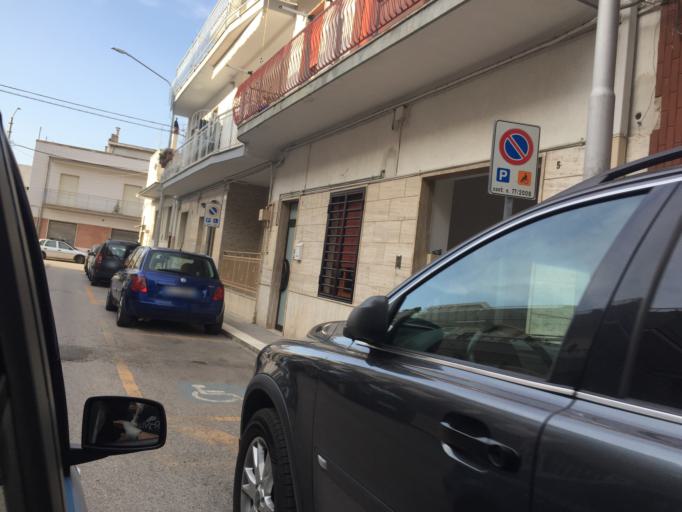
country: IT
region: Apulia
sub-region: Provincia di Bari
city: Capurso
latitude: 41.0482
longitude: 16.9172
